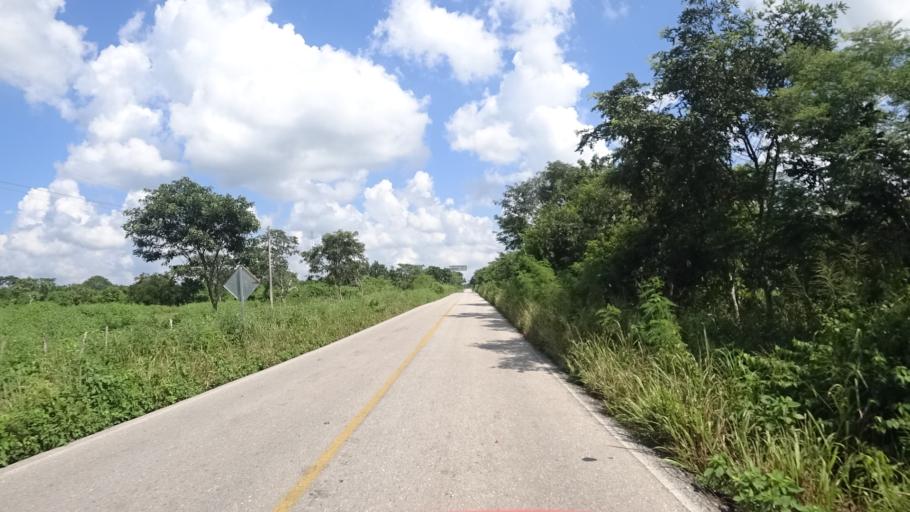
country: MX
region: Yucatan
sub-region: Panaba
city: Loche
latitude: 21.3828
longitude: -88.1425
